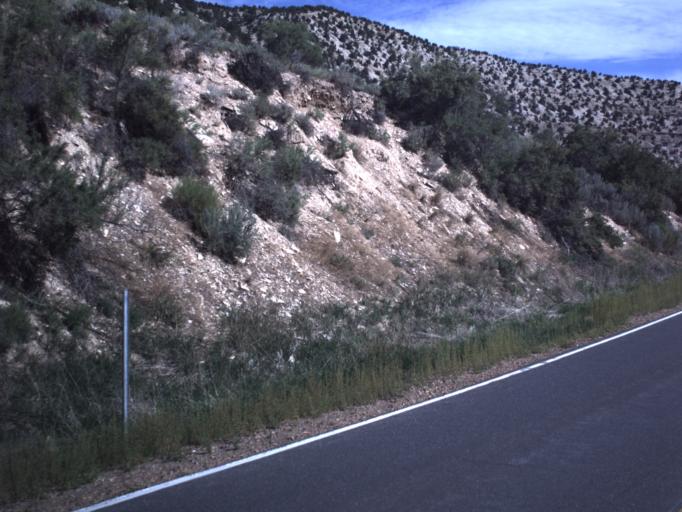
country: US
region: Utah
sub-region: Duchesne County
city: Duchesne
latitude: 40.0678
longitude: -110.5129
